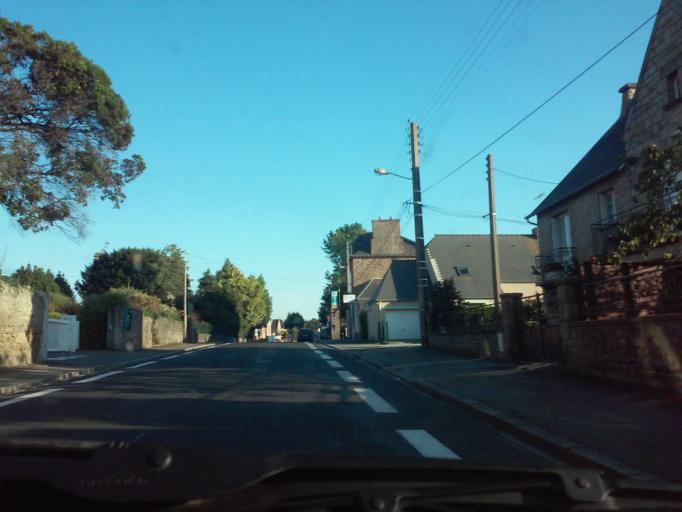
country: FR
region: Brittany
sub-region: Departement d'Ille-et-Vilaine
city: Dinard
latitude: 48.6245
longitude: -2.0594
